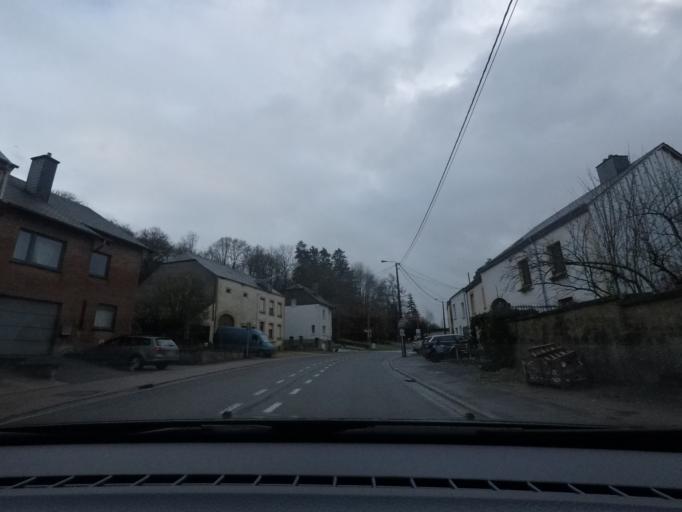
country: BE
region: Wallonia
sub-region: Province du Luxembourg
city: Tintigny
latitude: 49.7166
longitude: 5.4857
